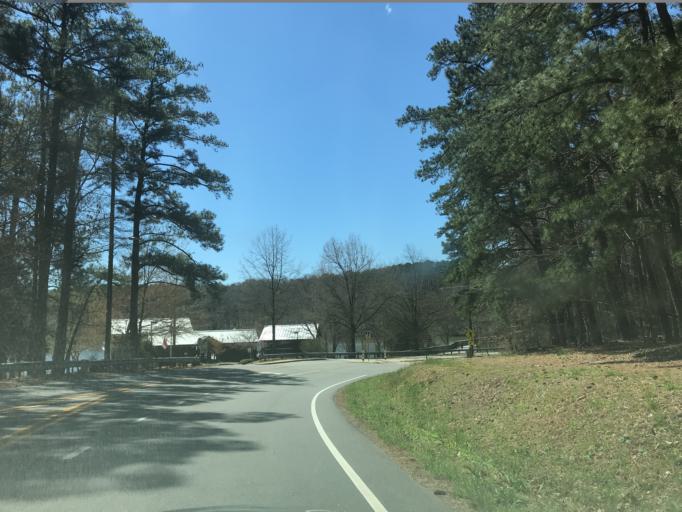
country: US
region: North Carolina
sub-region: Wake County
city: West Raleigh
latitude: 35.7634
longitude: -78.7142
